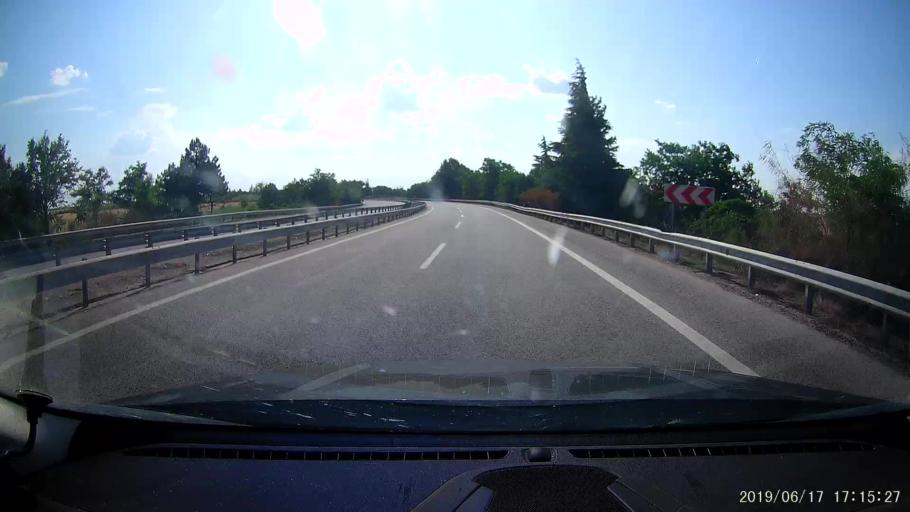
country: GR
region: East Macedonia and Thrace
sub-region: Nomos Evrou
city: Kastanies
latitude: 41.7021
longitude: 26.4961
